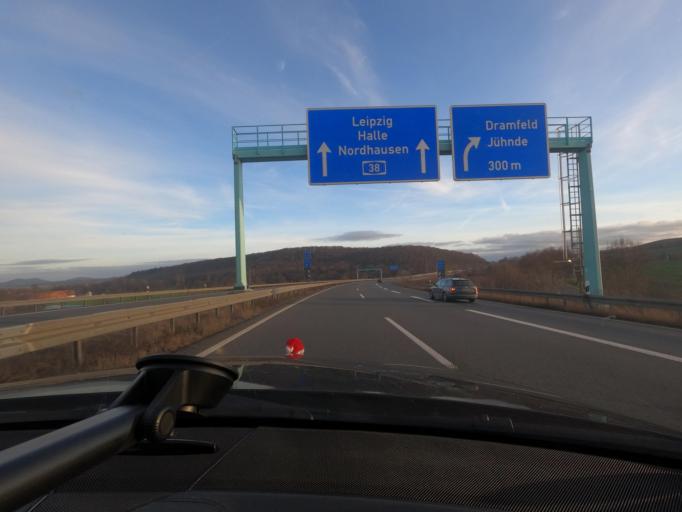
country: DE
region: Lower Saxony
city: Rosdorf
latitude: 51.4521
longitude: 9.8672
